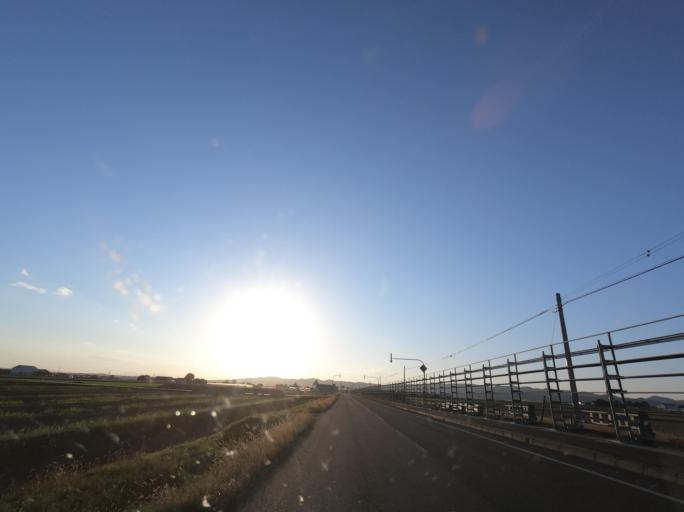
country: JP
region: Hokkaido
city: Iwamizawa
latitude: 42.9798
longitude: 141.8409
